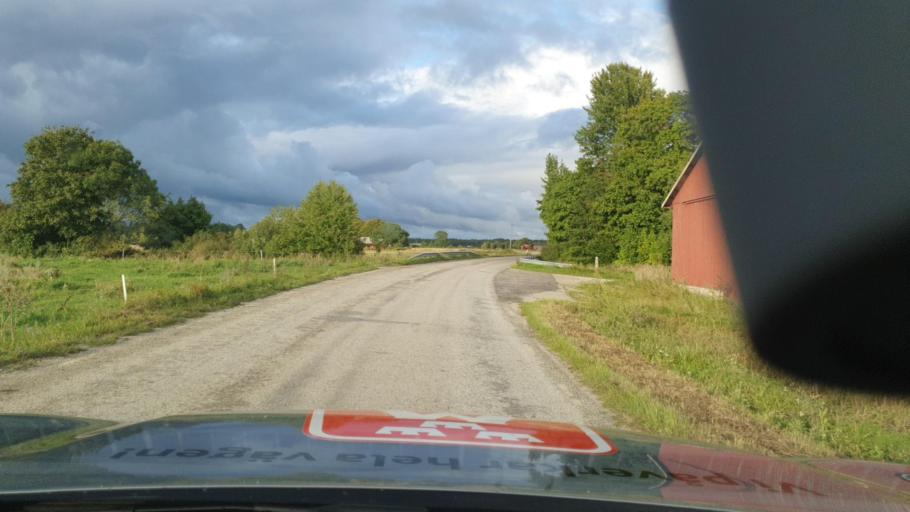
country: SE
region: Gotland
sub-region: Gotland
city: Klintehamn
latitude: 57.4568
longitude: 18.2169
